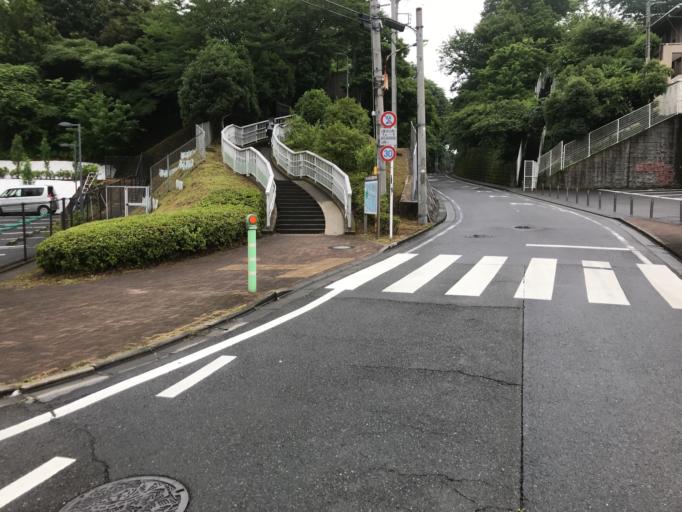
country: JP
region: Tokyo
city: Hachioji
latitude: 35.6686
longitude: 139.3412
